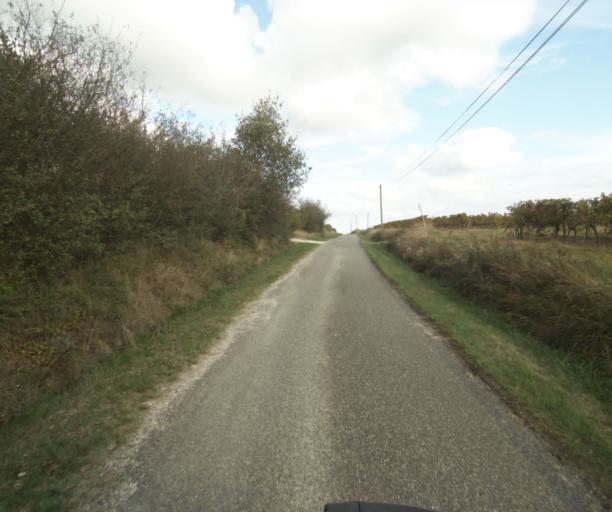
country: FR
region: Midi-Pyrenees
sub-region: Departement de la Haute-Garonne
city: Launac
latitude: 43.8255
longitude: 1.1050
